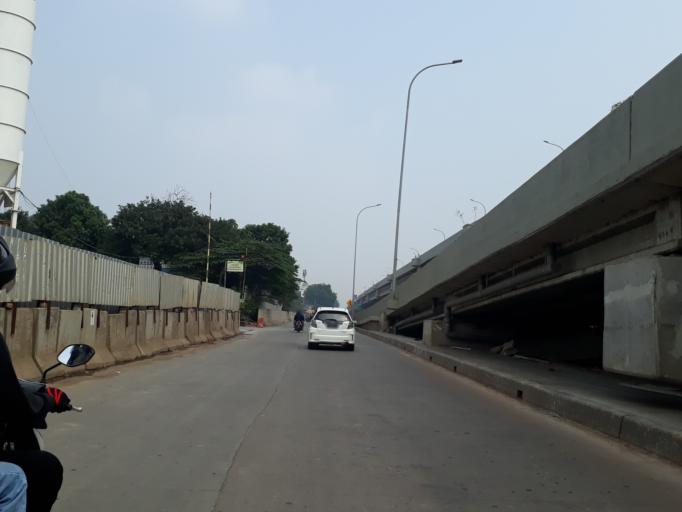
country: ID
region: West Java
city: Bekasi
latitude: -6.2499
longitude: 106.9392
